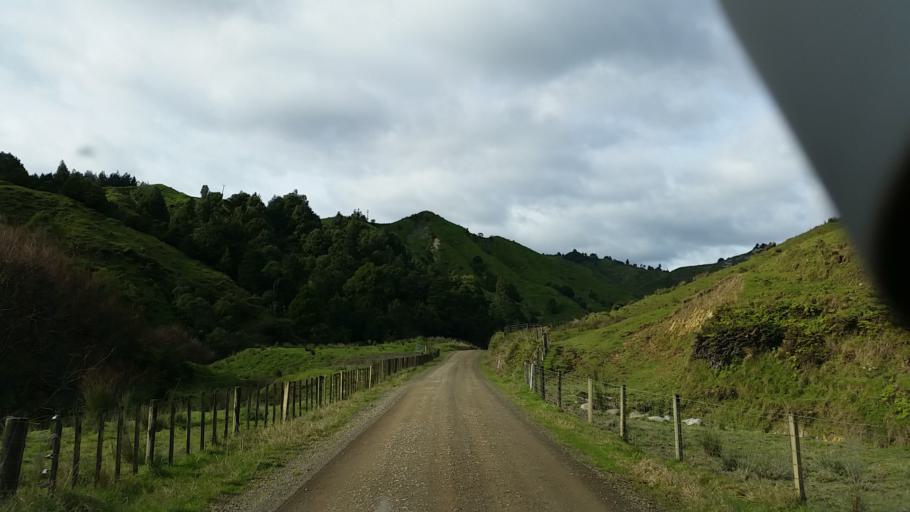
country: NZ
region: Taranaki
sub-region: New Plymouth District
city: Waitara
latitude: -39.0208
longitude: 174.5710
